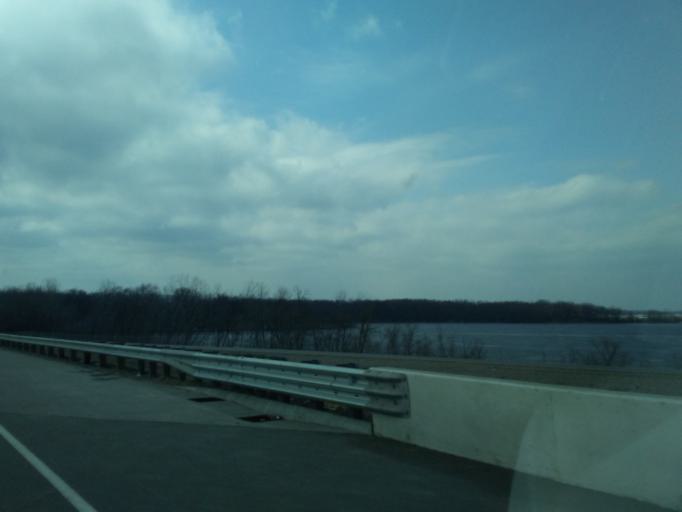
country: US
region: Wisconsin
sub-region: La Crosse County
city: Onalaska
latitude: 43.8645
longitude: -91.2373
